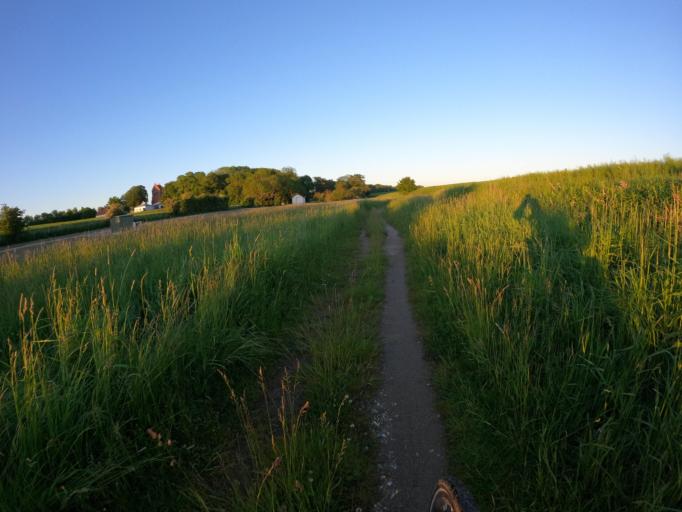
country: DK
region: Capital Region
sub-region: Hoje-Taastrup Kommune
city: Taastrup
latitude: 55.6251
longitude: 12.2422
